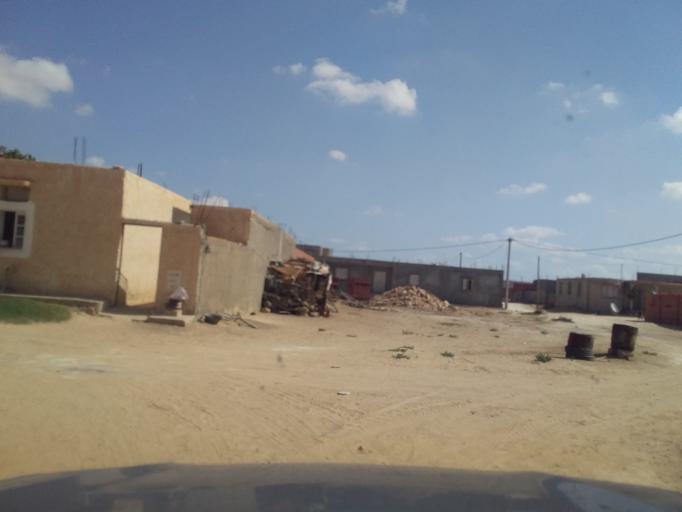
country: TN
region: Madanin
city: Medenine
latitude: 33.5807
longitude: 10.3268
